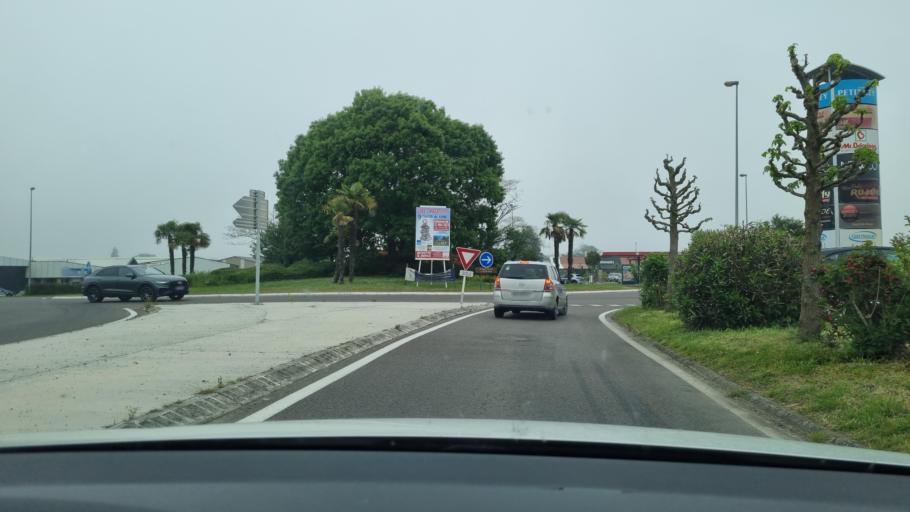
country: FR
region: Aquitaine
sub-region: Departement des Landes
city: Hagetmau
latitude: 43.6370
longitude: -0.6146
